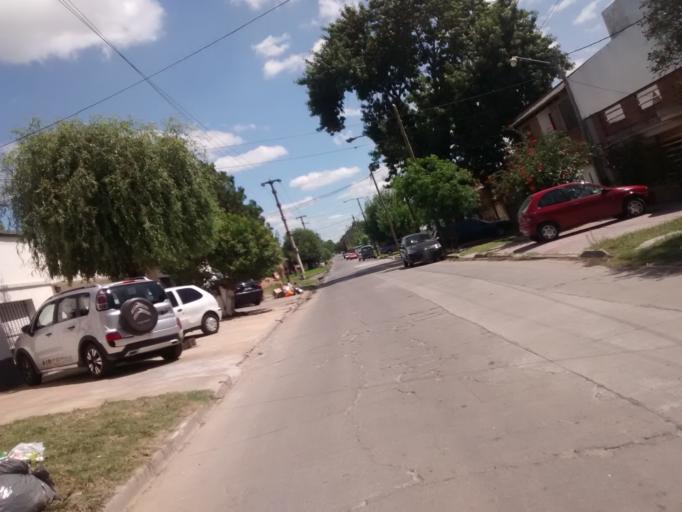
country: AR
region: Buenos Aires
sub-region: Partido de La Plata
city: La Plata
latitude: -34.9199
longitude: -57.9983
